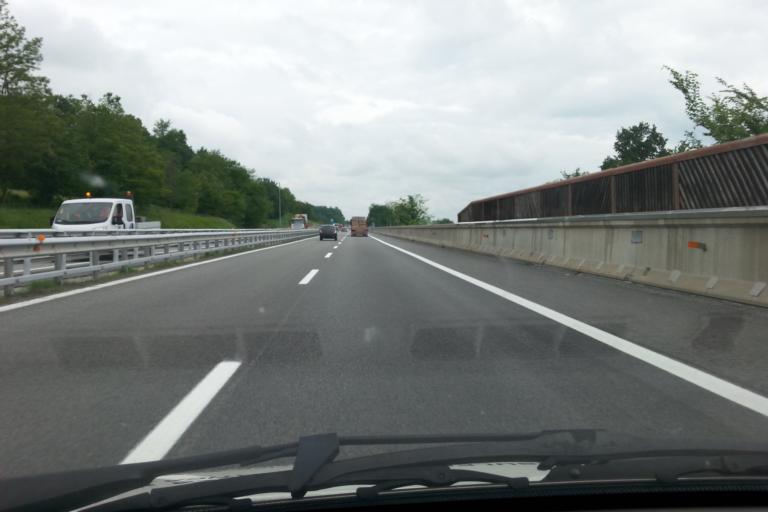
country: IT
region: Piedmont
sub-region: Provincia di Cuneo
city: Niella Tanaro
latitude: 44.4057
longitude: 7.9208
